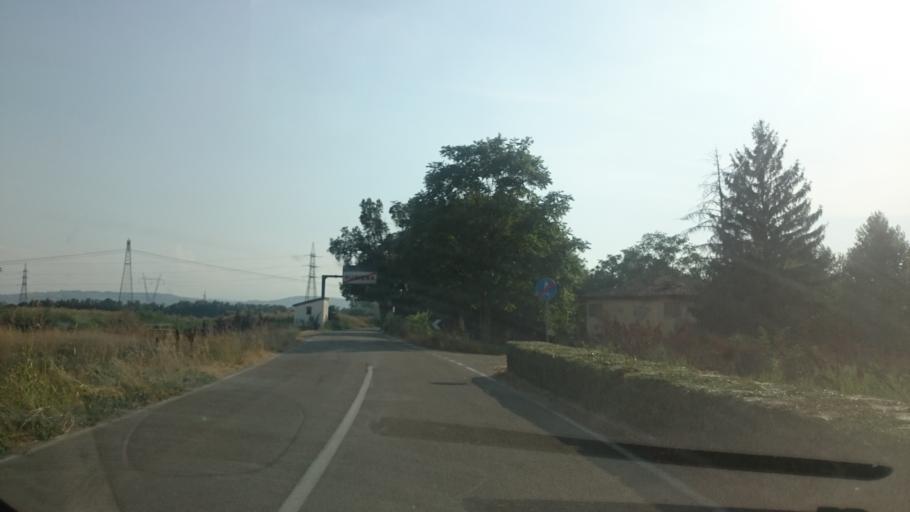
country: IT
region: Emilia-Romagna
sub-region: Provincia di Reggio Emilia
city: Rubiera
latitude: 44.6385
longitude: 10.7715
